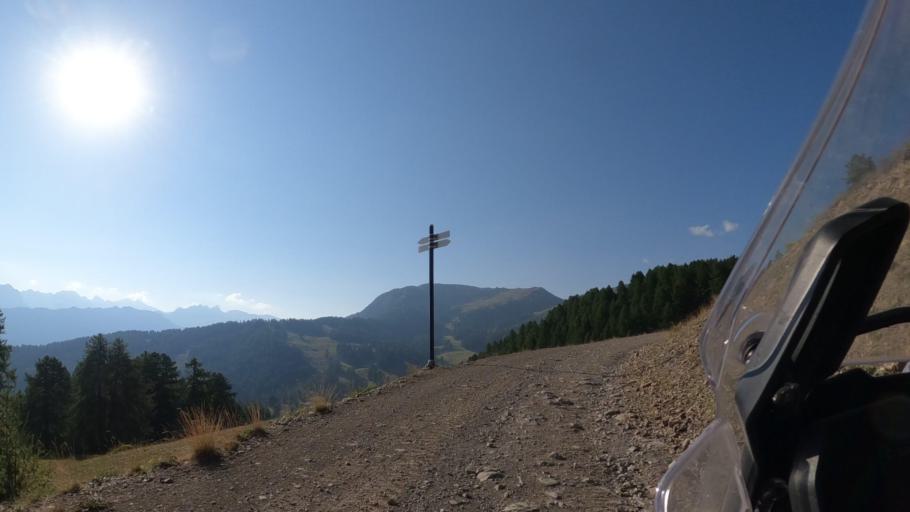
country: FR
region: Provence-Alpes-Cote d'Azur
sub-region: Departement des Hautes-Alpes
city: Guillestre
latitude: 44.6176
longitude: 6.6243
